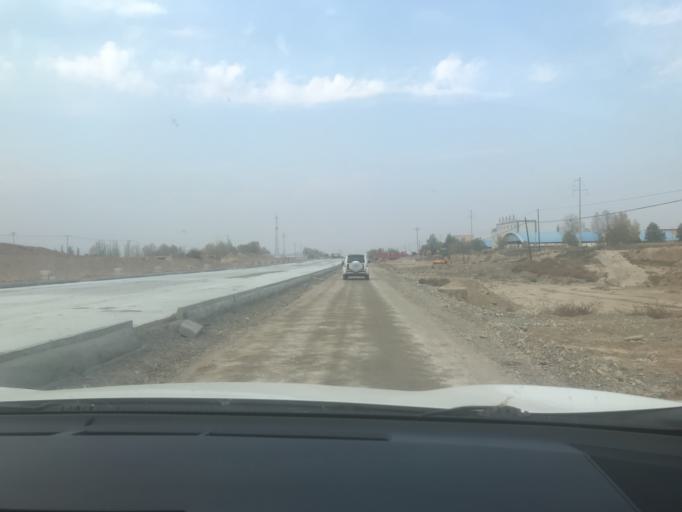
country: CN
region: Gansu Sheng
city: Gulang
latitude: 37.5124
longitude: 102.9010
